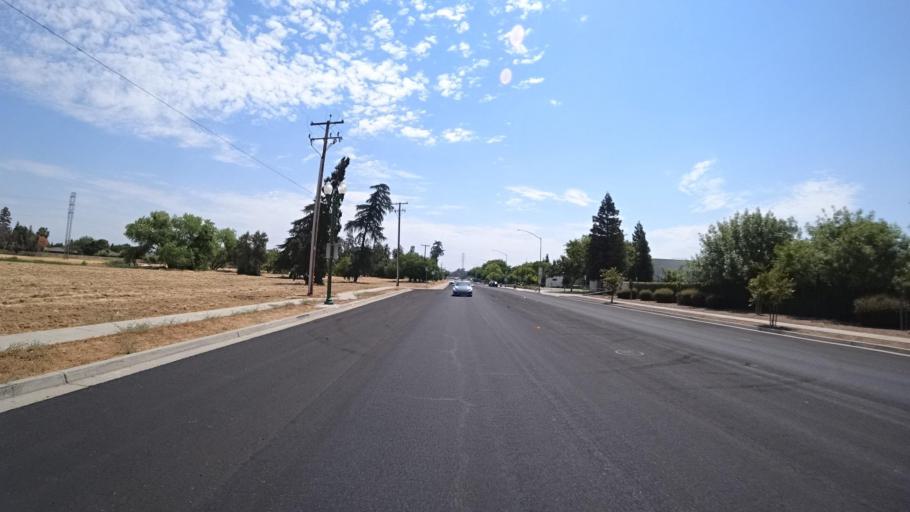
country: US
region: California
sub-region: Fresno County
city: Sunnyside
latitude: 36.7436
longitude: -119.6861
